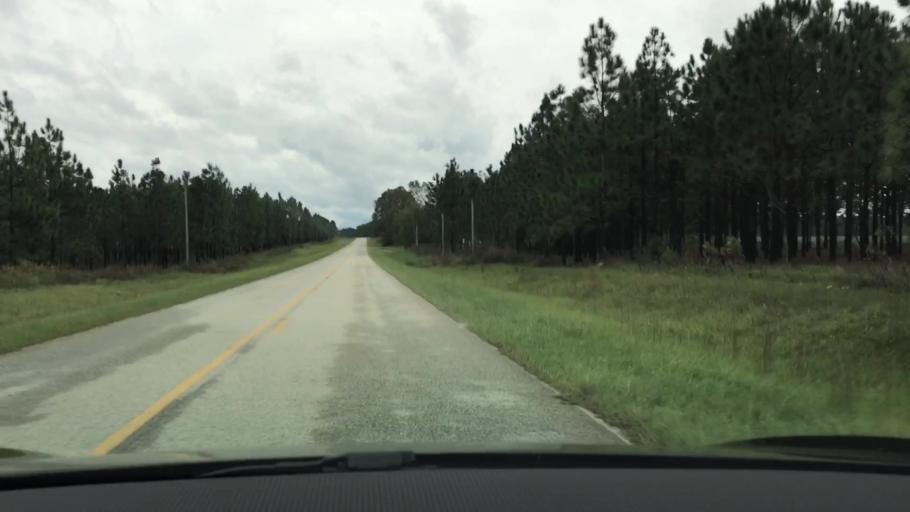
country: US
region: Georgia
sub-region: Jefferson County
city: Wadley
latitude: 32.8322
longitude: -82.3874
